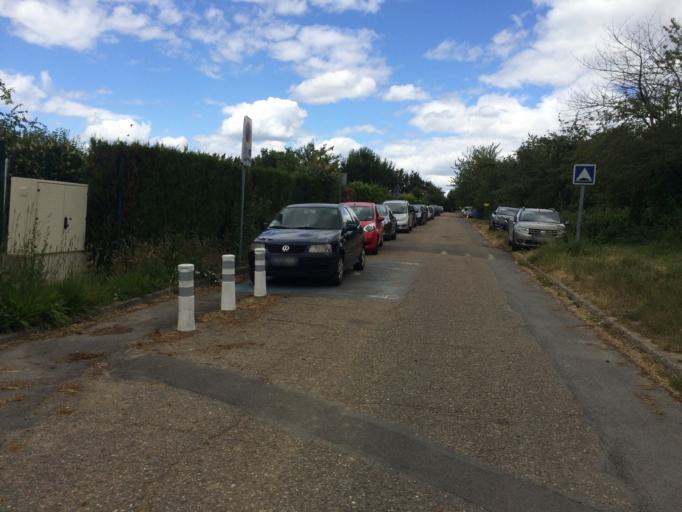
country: FR
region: Ile-de-France
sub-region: Departement de l'Essonne
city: Les Ulis
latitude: 48.6725
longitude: 2.1816
